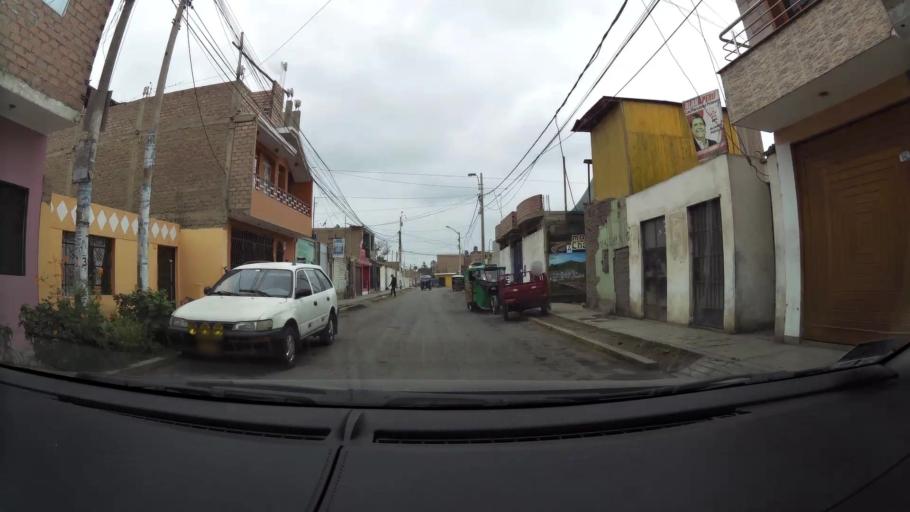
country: PE
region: Lima
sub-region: Provincia de Huaral
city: Huaral
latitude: -11.5006
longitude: -77.2149
